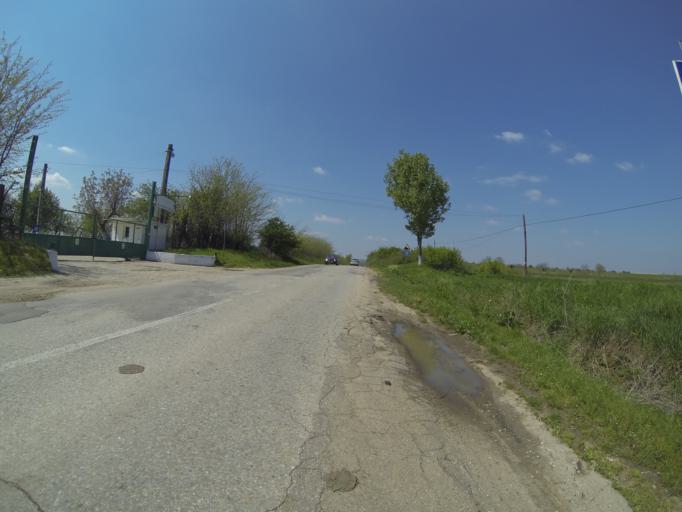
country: RO
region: Dolj
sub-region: Comuna Terpezita
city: Terpezita
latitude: 44.2925
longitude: 23.5216
